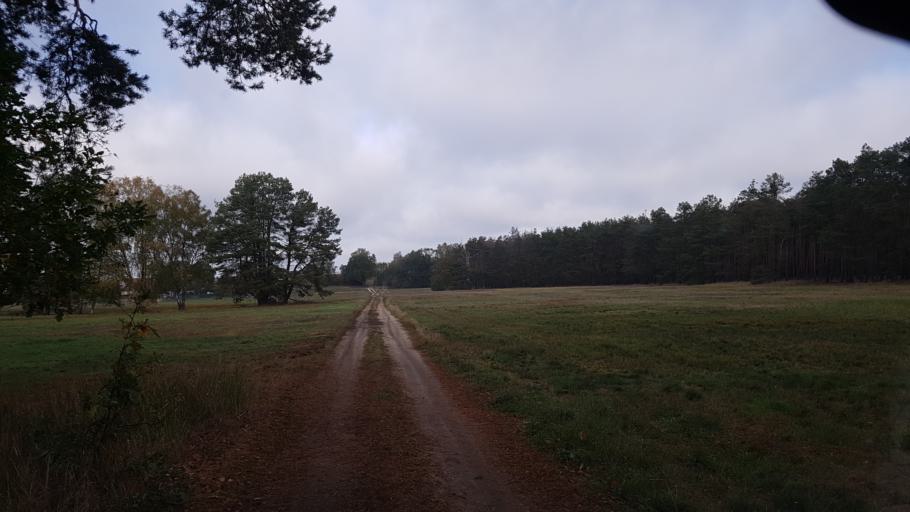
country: DE
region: Brandenburg
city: Schonborn
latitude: 51.6625
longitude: 13.4709
